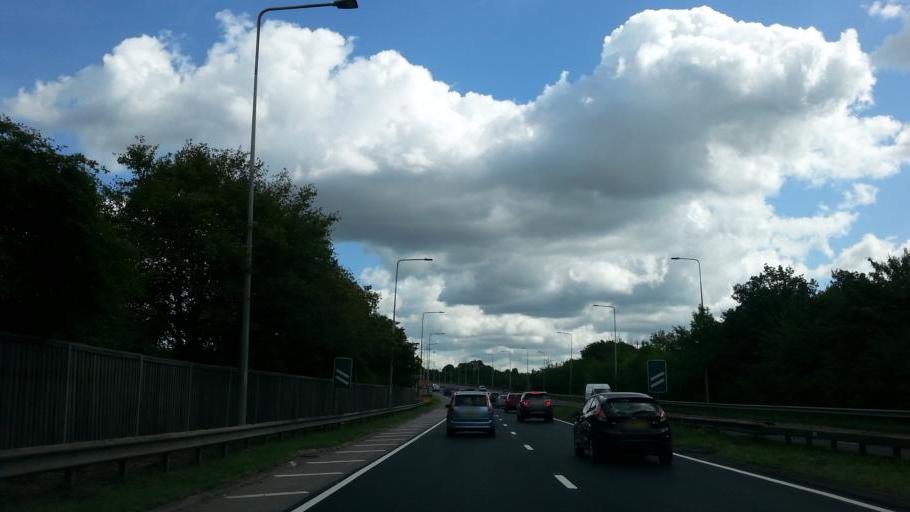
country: GB
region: England
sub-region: Essex
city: Pitsea
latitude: 51.5597
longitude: 0.4963
